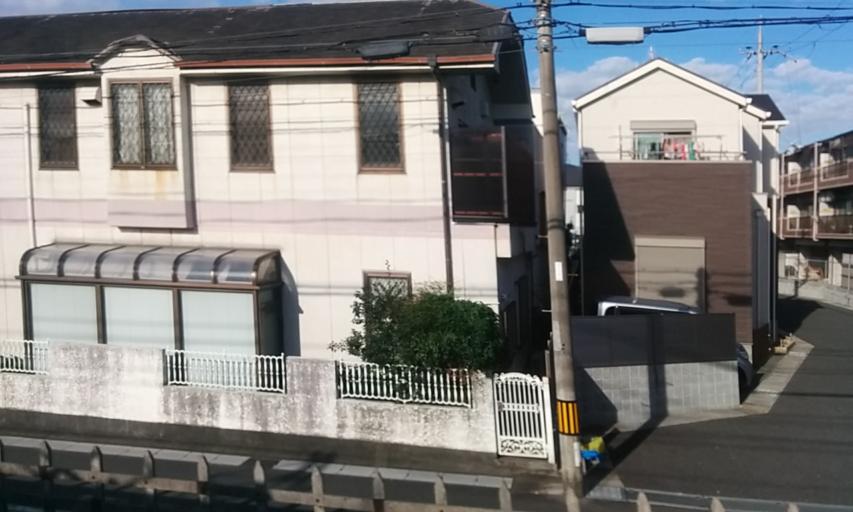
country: JP
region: Kyoto
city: Tanabe
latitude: 34.8612
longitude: 135.7740
